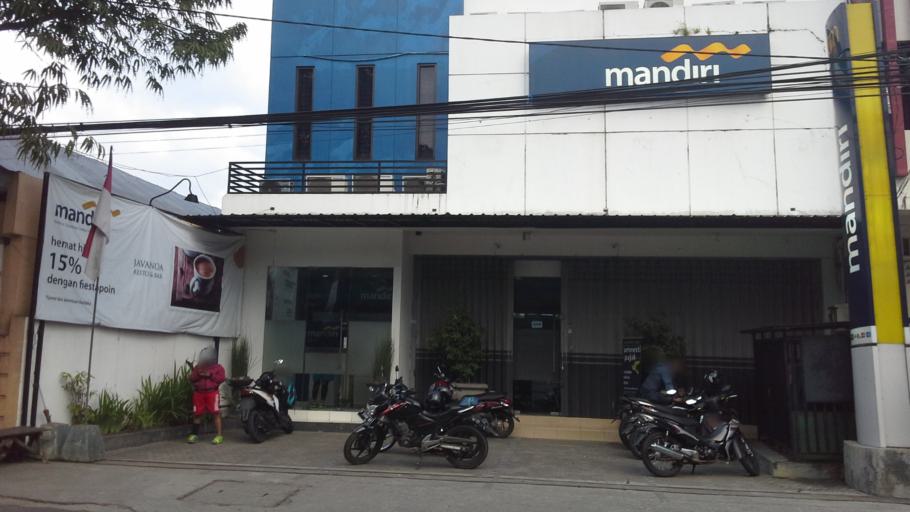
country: ID
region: East Java
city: Bondowoso
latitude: -7.9258
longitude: 113.8261
